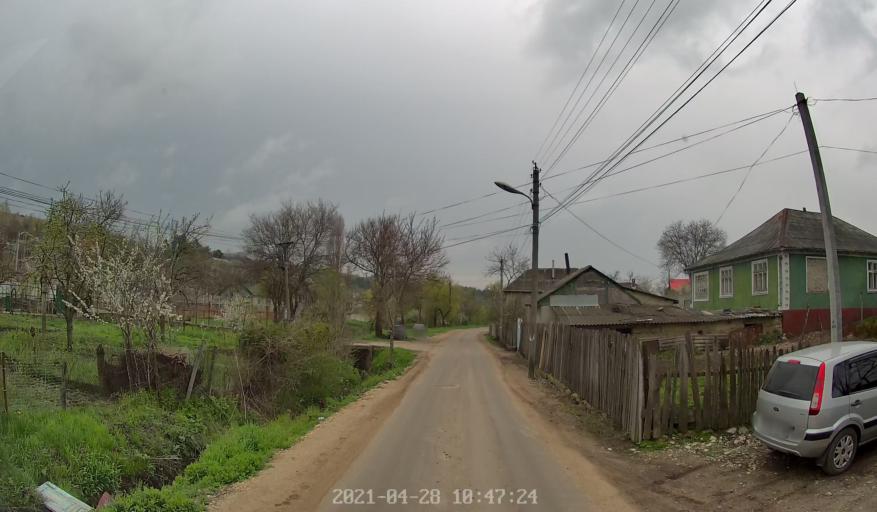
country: MD
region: Chisinau
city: Singera
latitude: 46.9892
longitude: 28.9480
